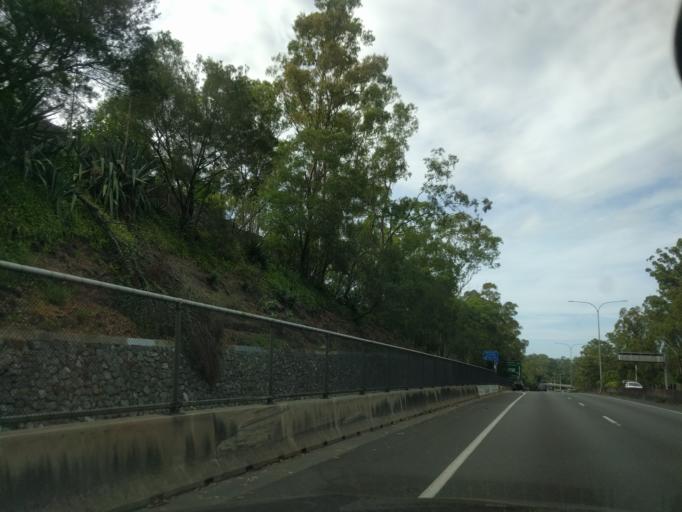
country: AU
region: Queensland
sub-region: Brisbane
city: Kenmore Hills
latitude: -27.5119
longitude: 152.9580
